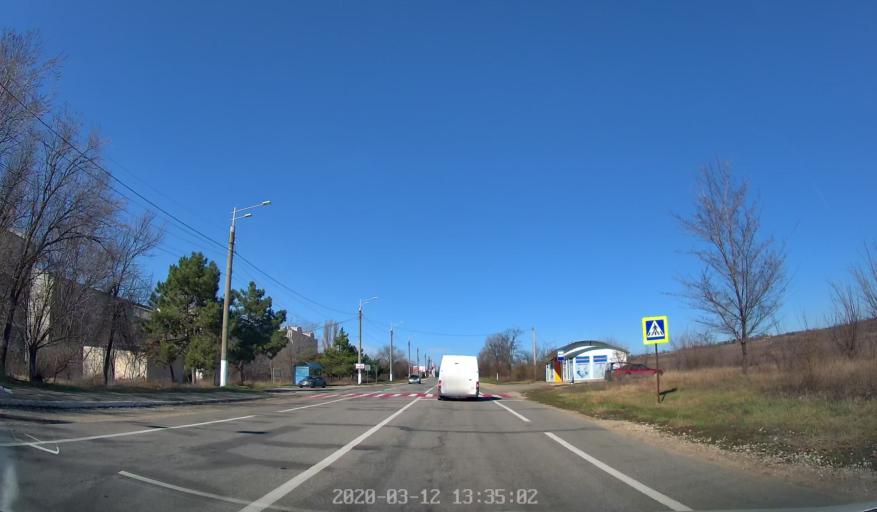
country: MD
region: Laloveni
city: Ialoveni
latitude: 46.9684
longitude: 28.7665
